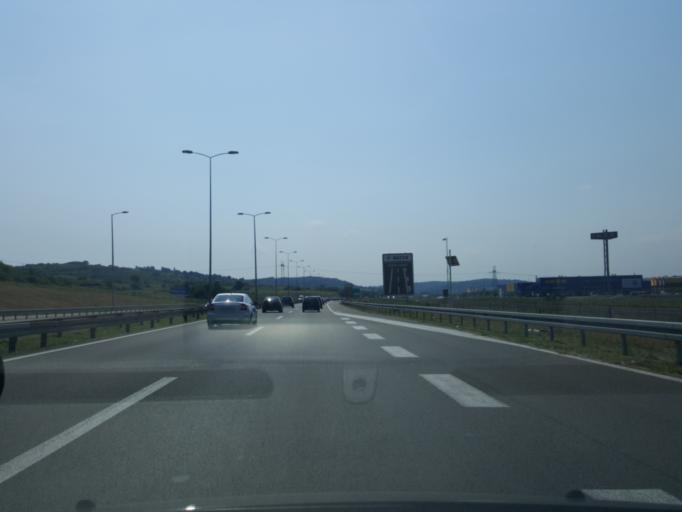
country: RS
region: Central Serbia
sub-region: Belgrade
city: Zvezdara
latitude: 44.7156
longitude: 20.5587
